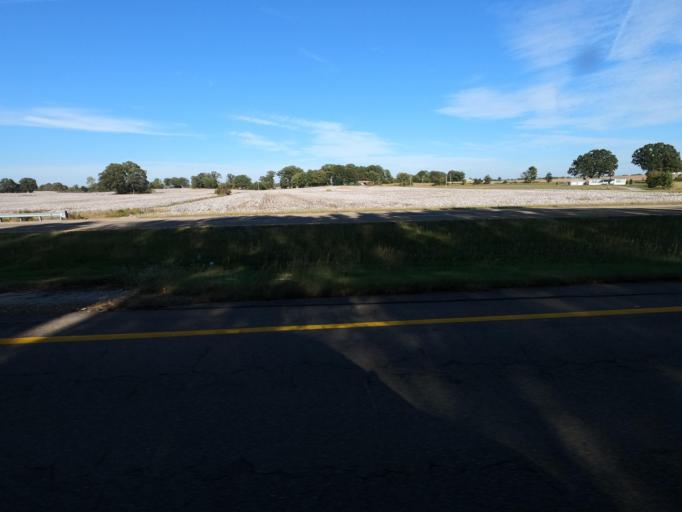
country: US
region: Tennessee
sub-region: Crockett County
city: Alamo
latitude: 35.8632
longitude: -89.2083
